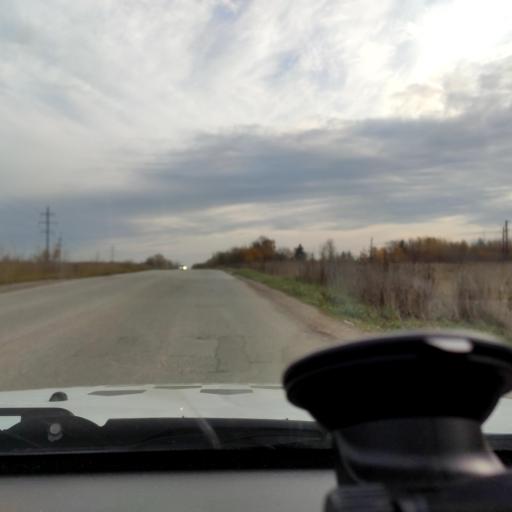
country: RU
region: Perm
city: Perm
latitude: 58.0148
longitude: 56.3295
